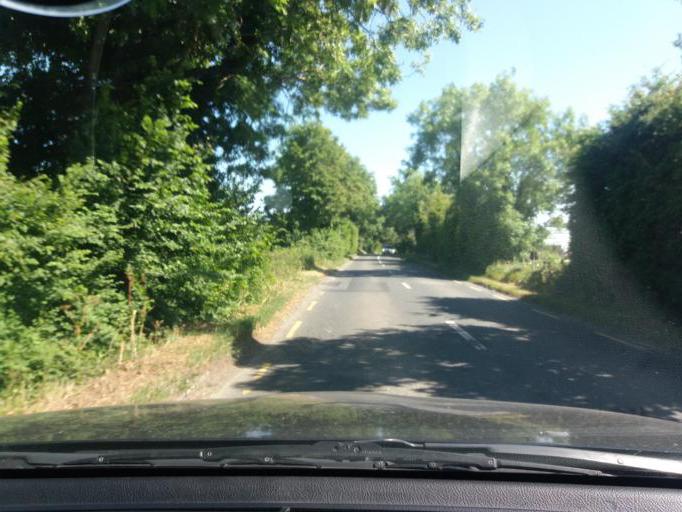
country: IE
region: Leinster
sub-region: Fingal County
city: Swords
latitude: 53.4610
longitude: -6.2697
